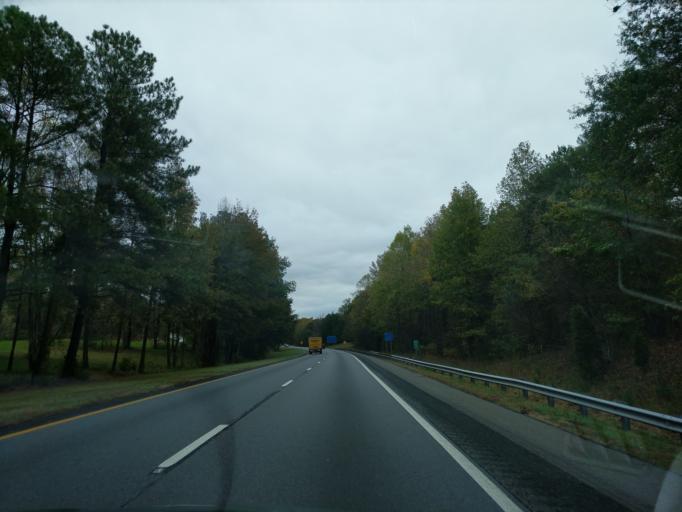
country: US
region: North Carolina
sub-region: Cleveland County
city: White Plains
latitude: 35.1709
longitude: -81.4291
